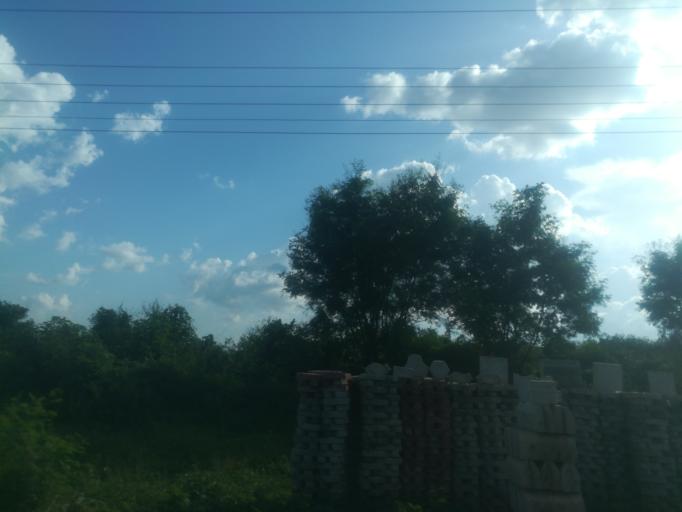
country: NG
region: Oyo
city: Ibadan
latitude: 7.4361
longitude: 3.9722
